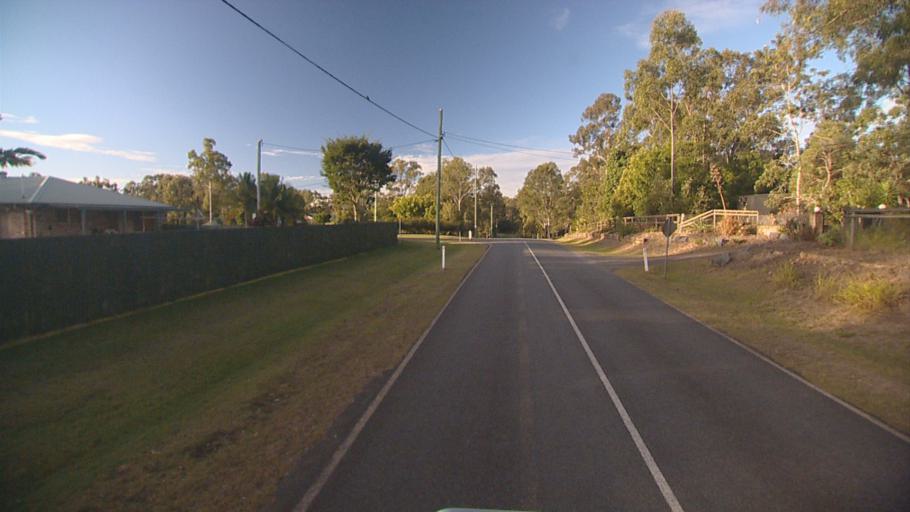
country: AU
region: Queensland
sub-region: Logan
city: Waterford West
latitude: -27.7300
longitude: 153.1385
